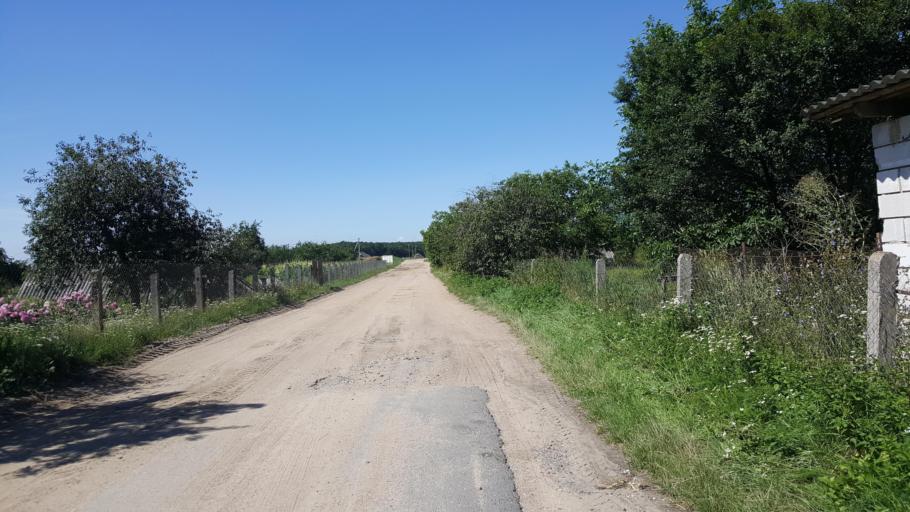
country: BY
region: Brest
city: Charnawchytsy
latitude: 52.2185
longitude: 23.7392
